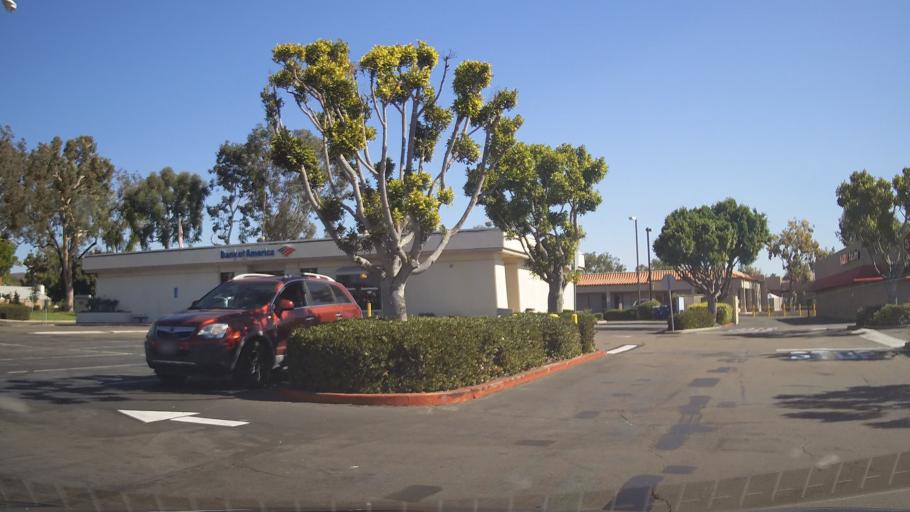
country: US
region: California
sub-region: San Diego County
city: La Mesa
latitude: 32.8222
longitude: -117.1006
